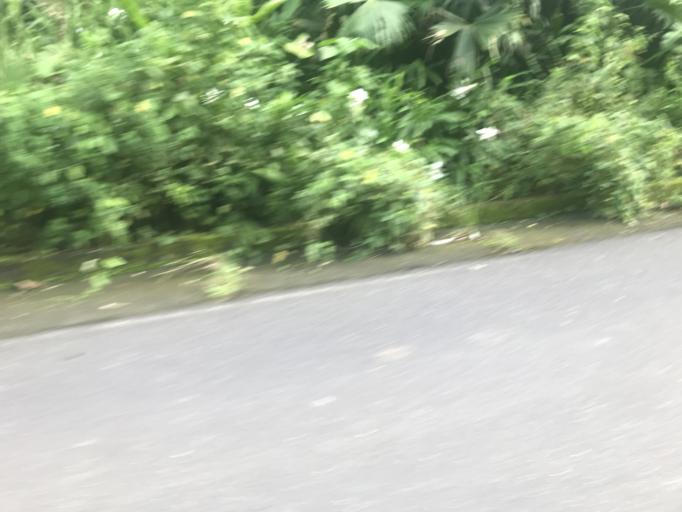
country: EC
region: Napo
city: Tena
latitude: -1.0423
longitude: -77.8000
